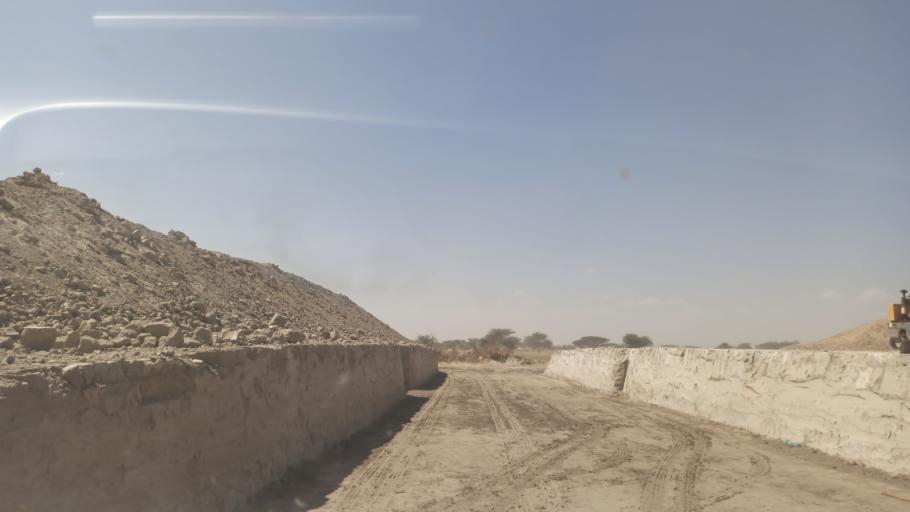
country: ET
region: Oromiya
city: Ziway
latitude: 7.7313
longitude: 38.6255
